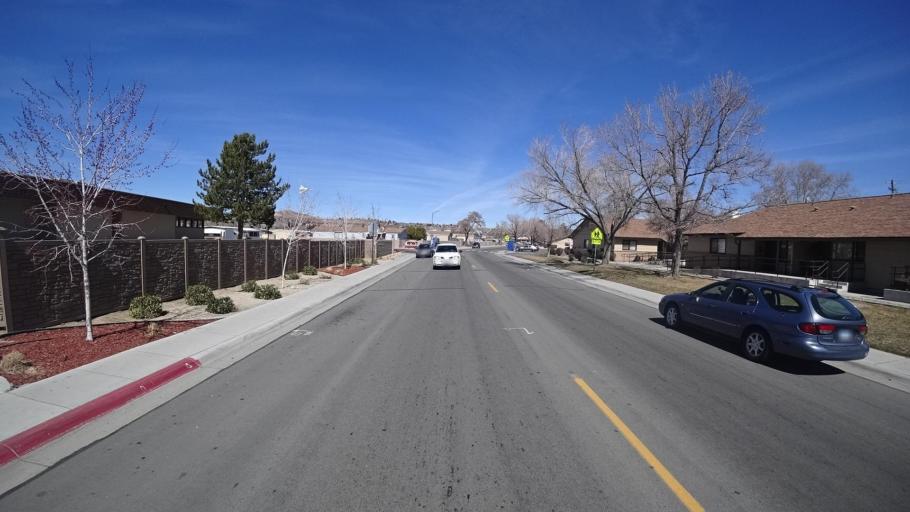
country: US
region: Nevada
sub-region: Washoe County
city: Sparks
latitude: 39.5424
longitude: -119.7840
